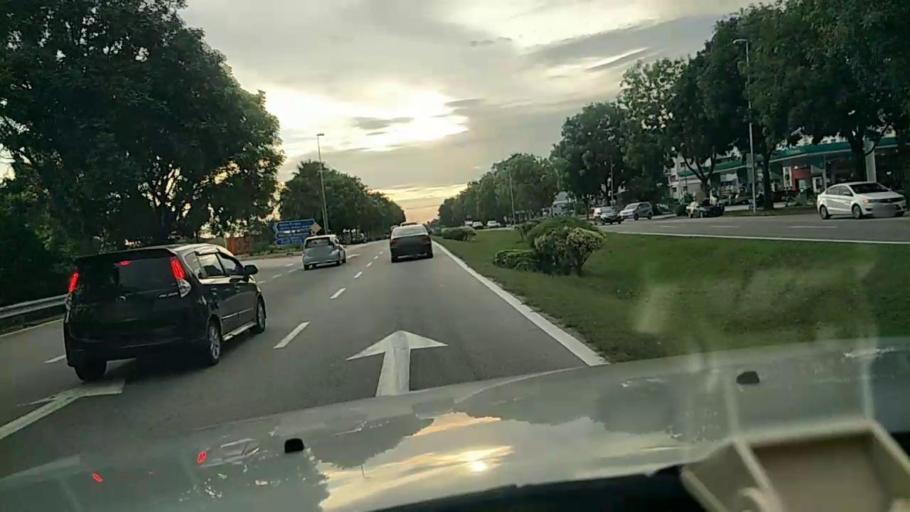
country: MY
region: Selangor
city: Klang
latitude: 3.1086
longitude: 101.4488
